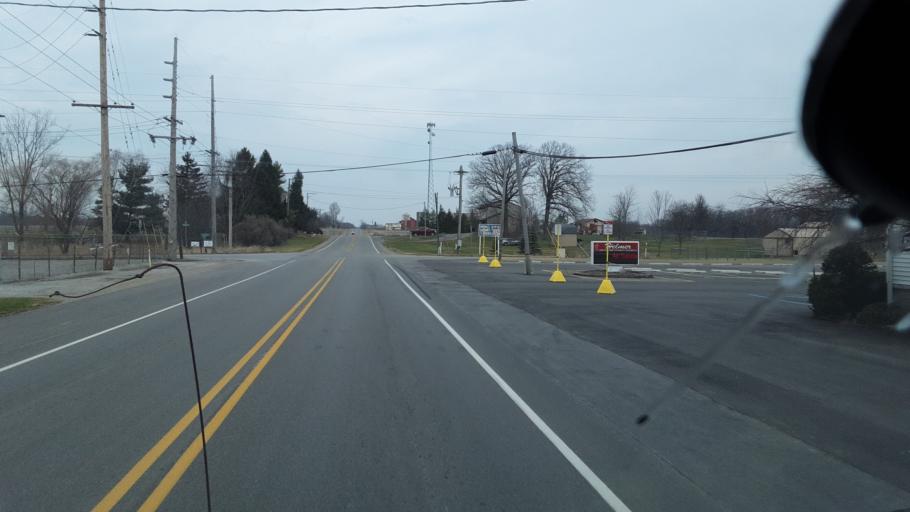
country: US
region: Indiana
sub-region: Noble County
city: Kendallville
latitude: 41.5332
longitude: -85.1706
